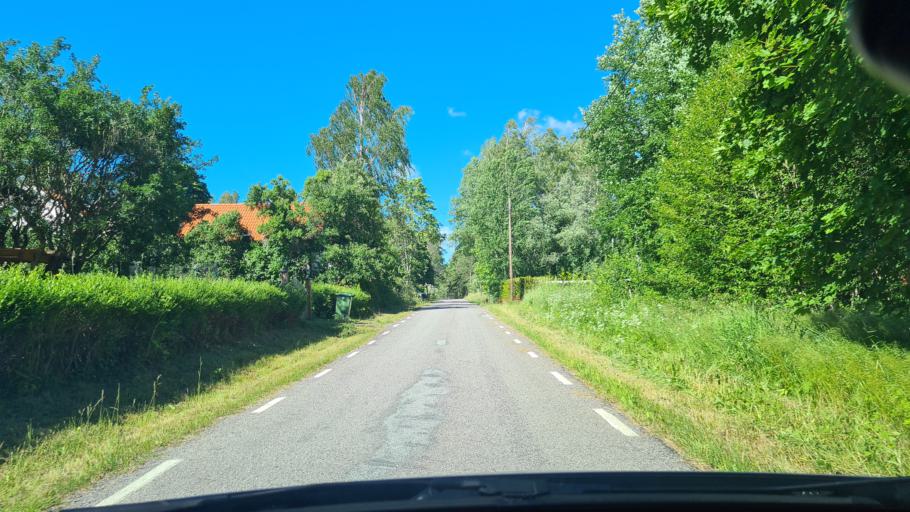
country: SE
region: OEstergoetland
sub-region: Norrkopings Kommun
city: Krokek
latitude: 58.7178
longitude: 16.4293
